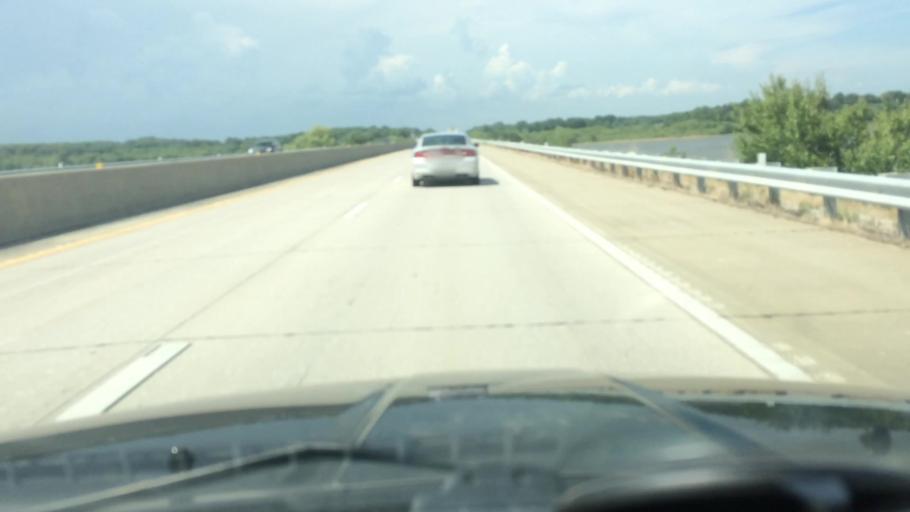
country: US
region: Missouri
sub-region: Henry County
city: Clinton
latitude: 38.2821
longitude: -93.7594
